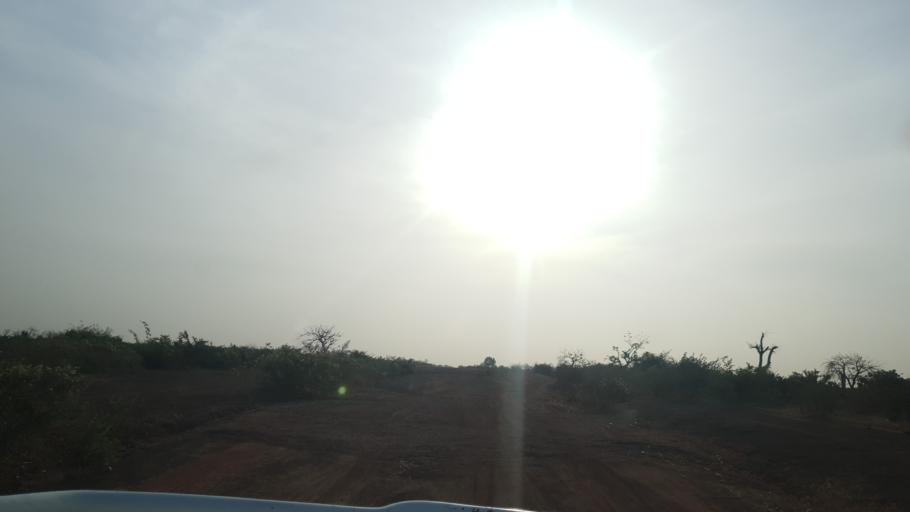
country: ML
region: Koulikoro
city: Dioila
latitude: 12.7675
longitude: -6.9219
